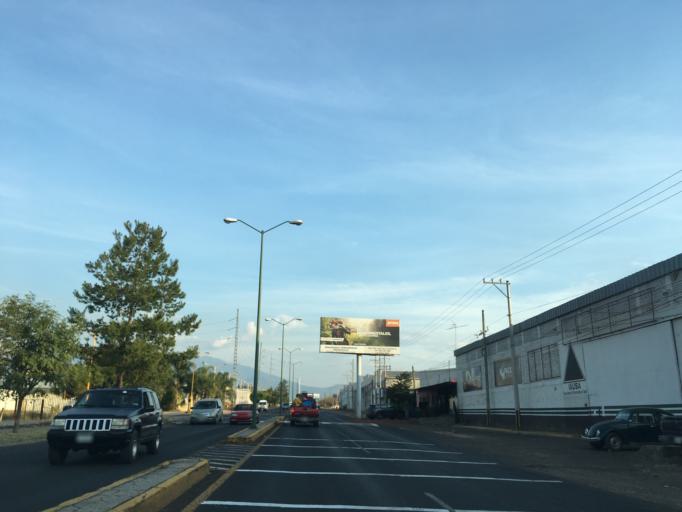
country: MX
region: Michoacan
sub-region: Los Reyes
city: La Higuerita (Colonia San Rafael)
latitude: 19.6052
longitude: -102.4783
